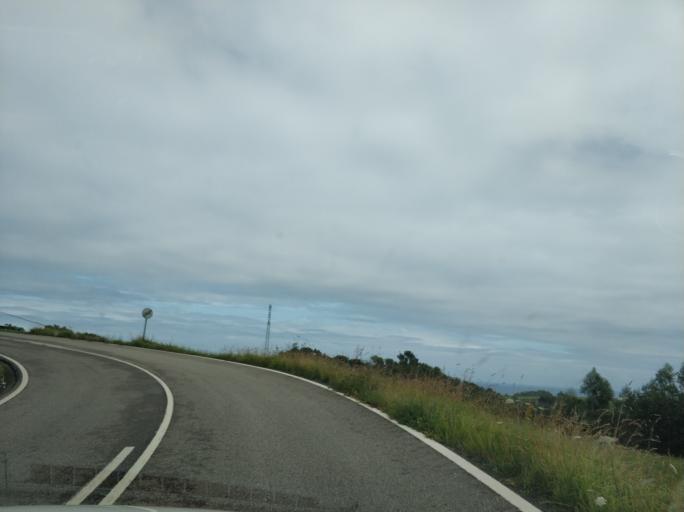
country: ES
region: Asturias
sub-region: Province of Asturias
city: Cudillero
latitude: 43.5606
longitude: -6.2933
